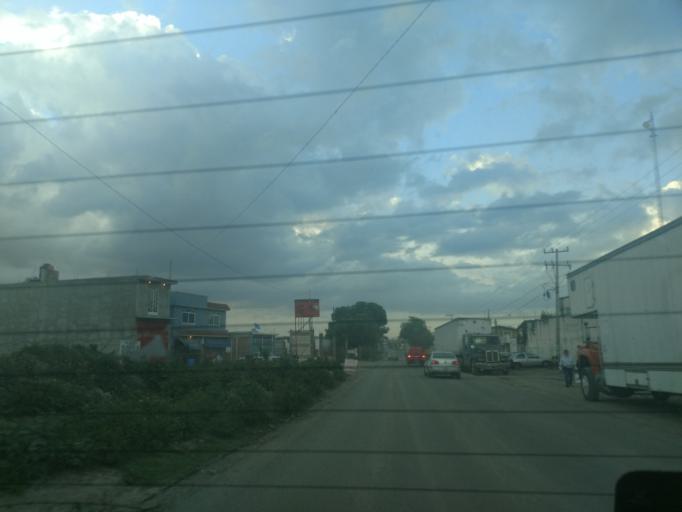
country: MX
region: Mexico
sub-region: Cuautitlan
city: Barrio Tlatenco
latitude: 19.7482
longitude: -99.2001
